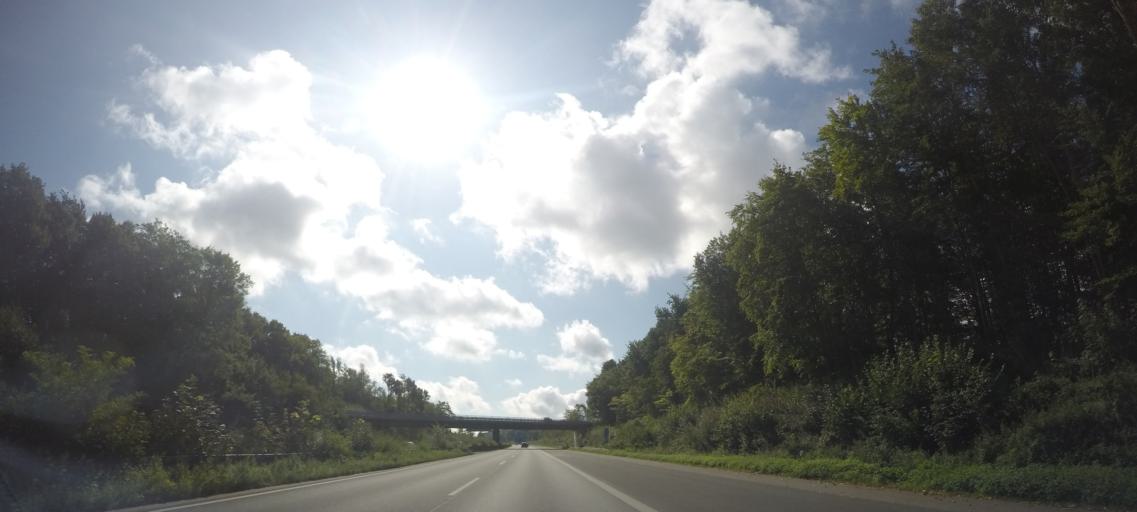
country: DE
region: North Rhine-Westphalia
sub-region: Regierungsbezirk Arnsberg
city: Werl
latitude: 51.5267
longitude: 7.8950
